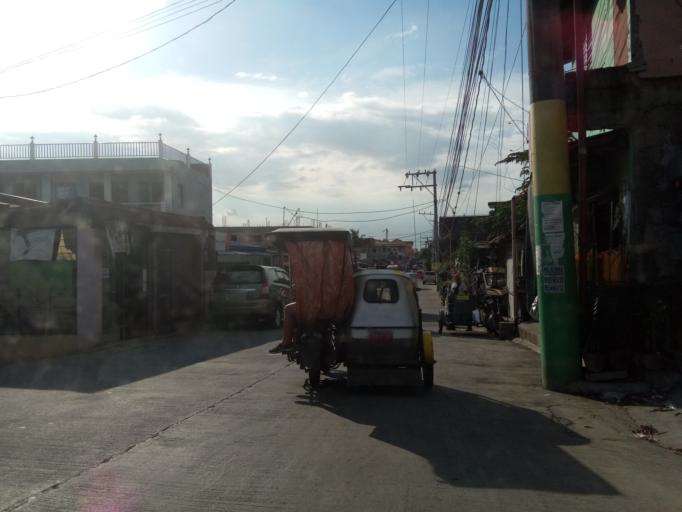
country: PH
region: Calabarzon
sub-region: Province of Cavite
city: Dasmarinas
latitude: 14.2906
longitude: 120.9407
